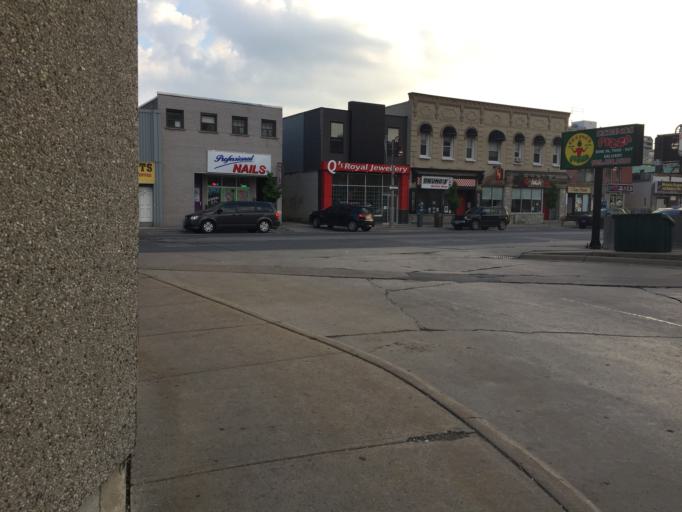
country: CA
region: Ontario
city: Oshawa
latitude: 43.8981
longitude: -78.8649
